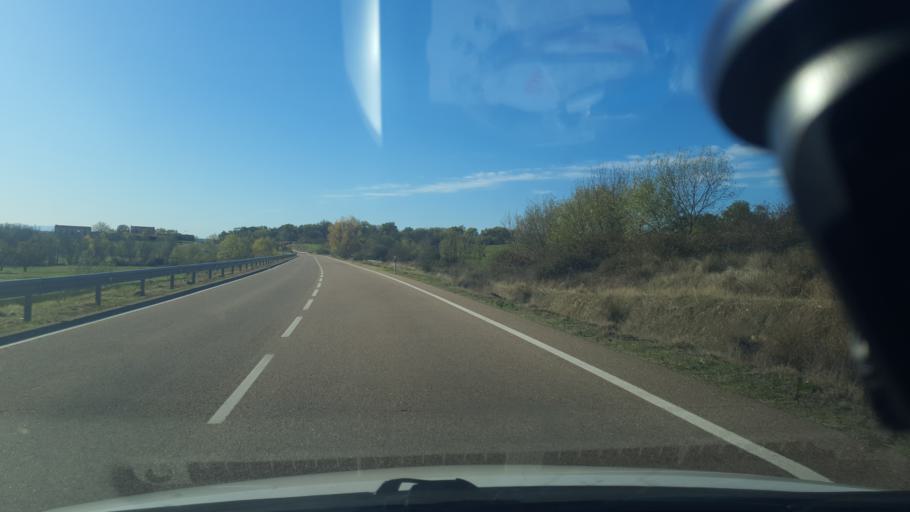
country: ES
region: Castille and Leon
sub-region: Provincia de Avila
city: Poyales del Hoyo
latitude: 40.1551
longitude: -5.1870
